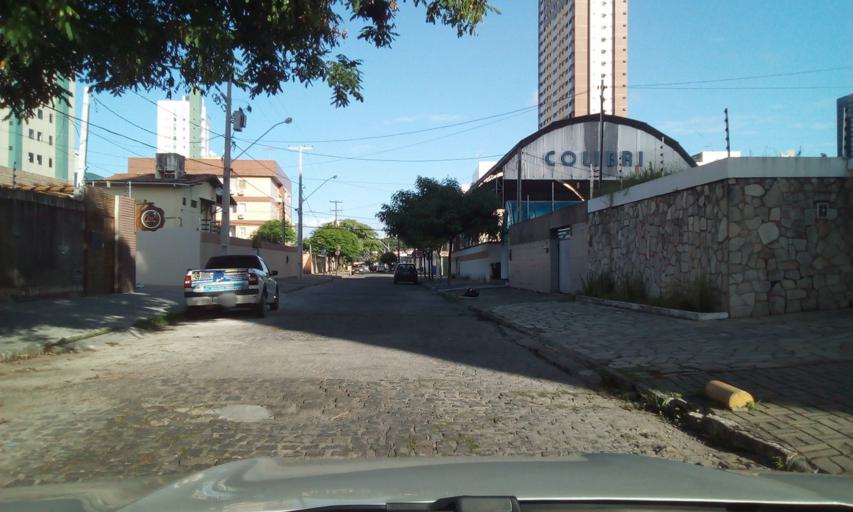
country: BR
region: Paraiba
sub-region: Joao Pessoa
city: Joao Pessoa
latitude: -7.1050
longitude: -34.8400
